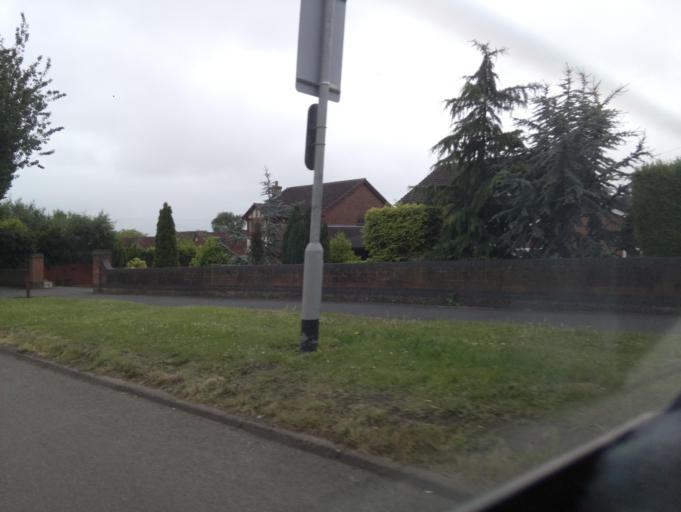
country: GB
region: England
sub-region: Staffordshire
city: Burton upon Trent
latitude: 52.7869
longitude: -1.6173
